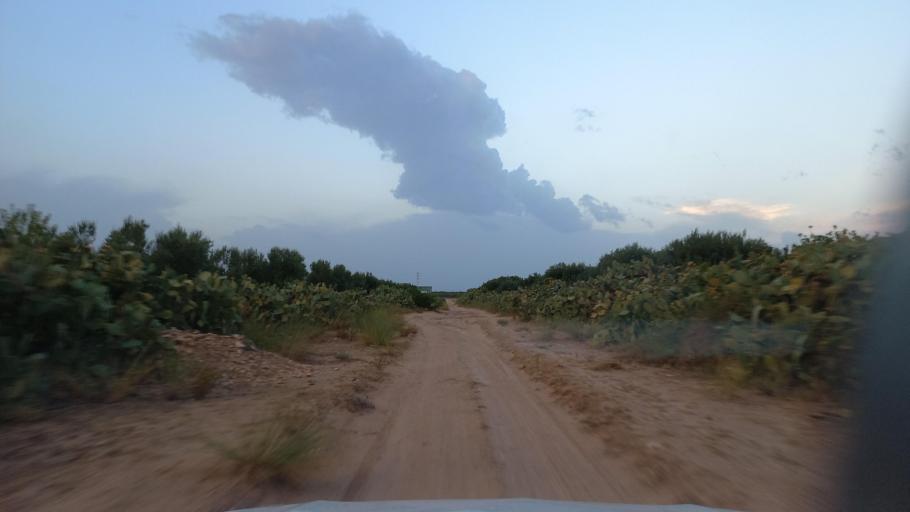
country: TN
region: Al Qasrayn
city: Kasserine
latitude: 35.2788
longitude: 9.0396
